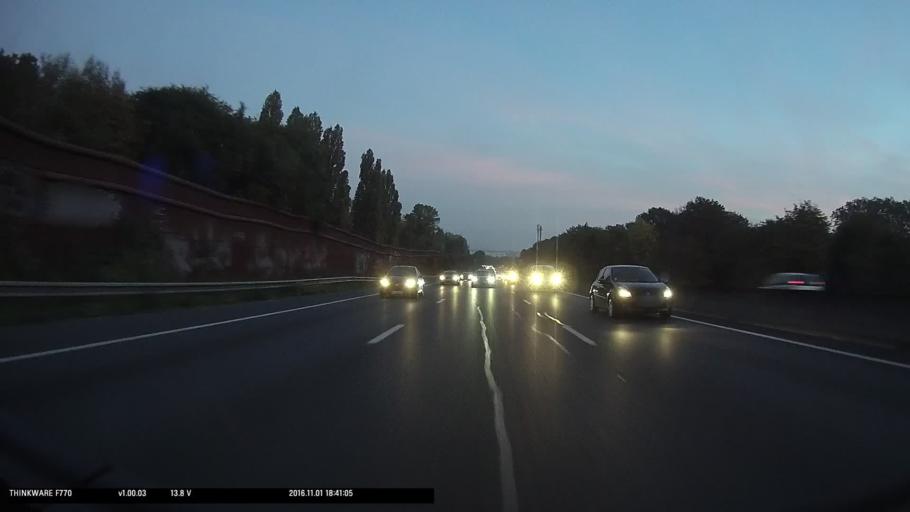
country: FR
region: Ile-de-France
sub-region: Departement de l'Essonne
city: Longjumeau
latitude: 48.6873
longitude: 2.3259
